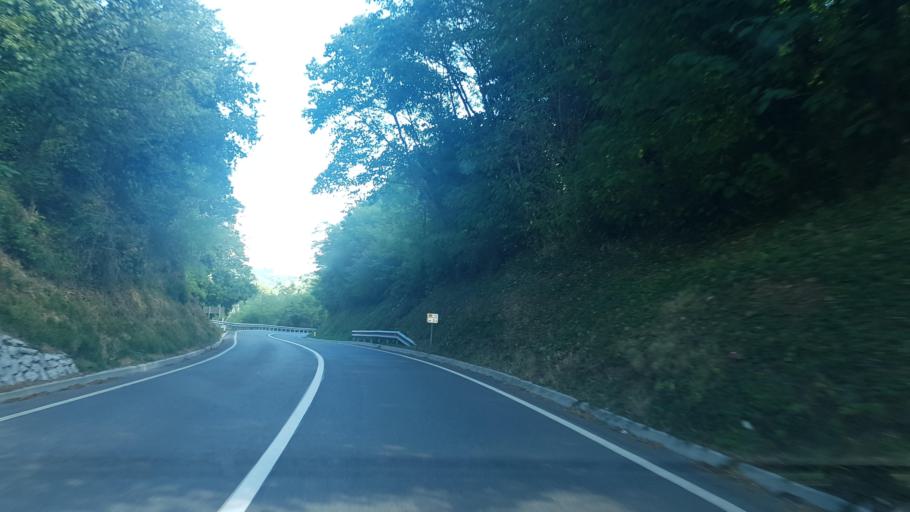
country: SI
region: Nova Gorica
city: Prvacina
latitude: 45.8829
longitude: 13.7389
